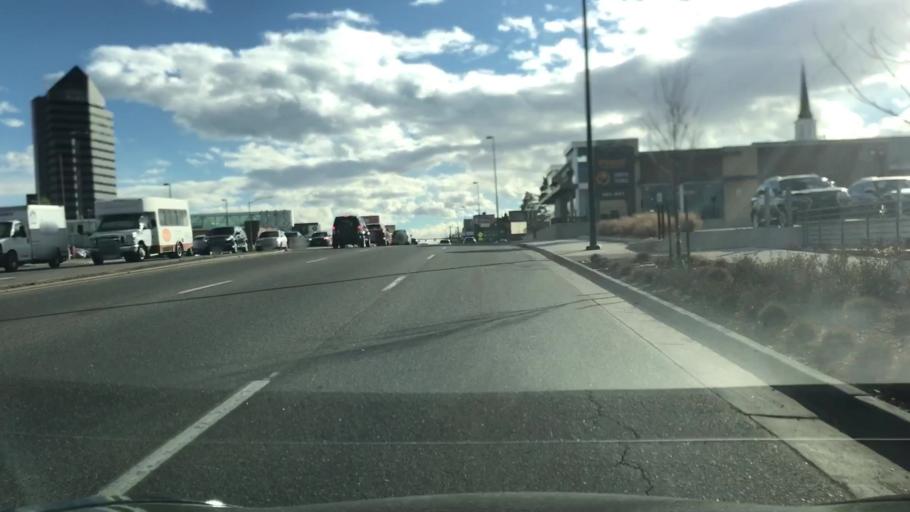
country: US
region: Colorado
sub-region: Arapahoe County
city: Glendale
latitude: 39.6996
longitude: -104.9408
